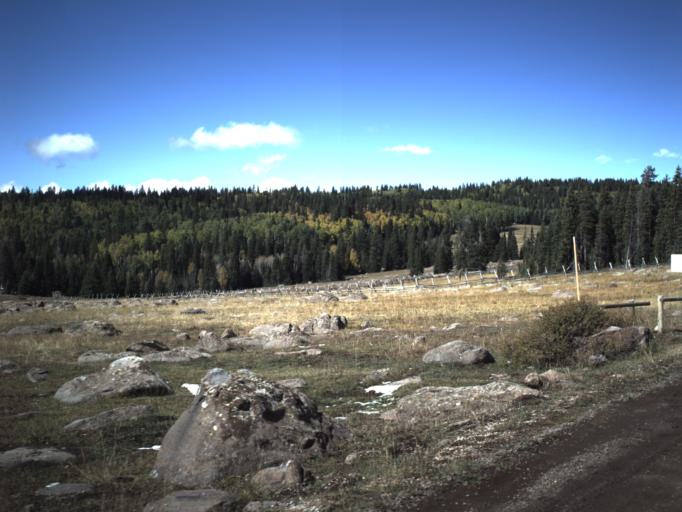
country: US
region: Utah
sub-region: Piute County
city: Junction
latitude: 38.2854
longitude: -112.3578
